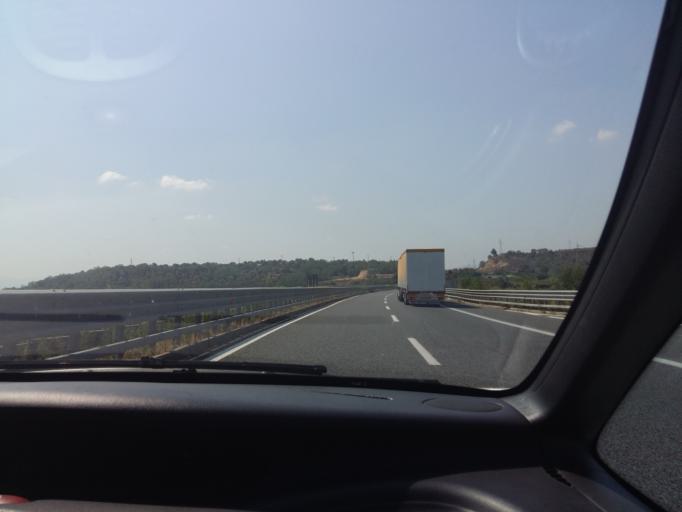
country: IT
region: Calabria
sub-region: Provincia di Reggio Calabria
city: Rosarno
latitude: 38.4908
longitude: 16.0096
